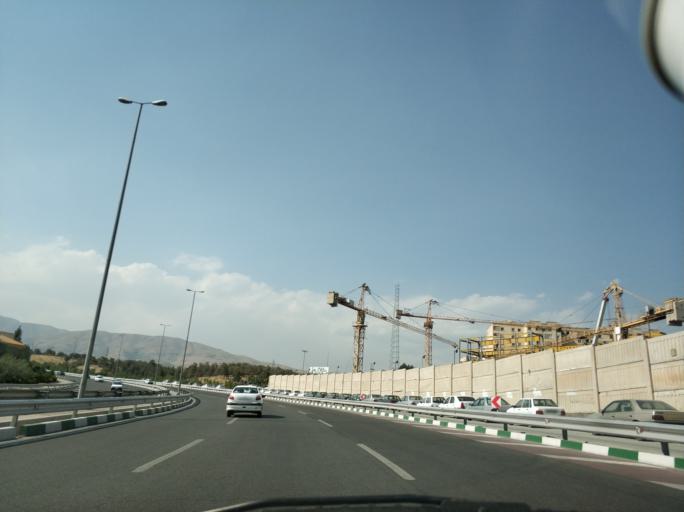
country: IR
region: Tehran
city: Tajrish
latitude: 35.7629
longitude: 51.5381
